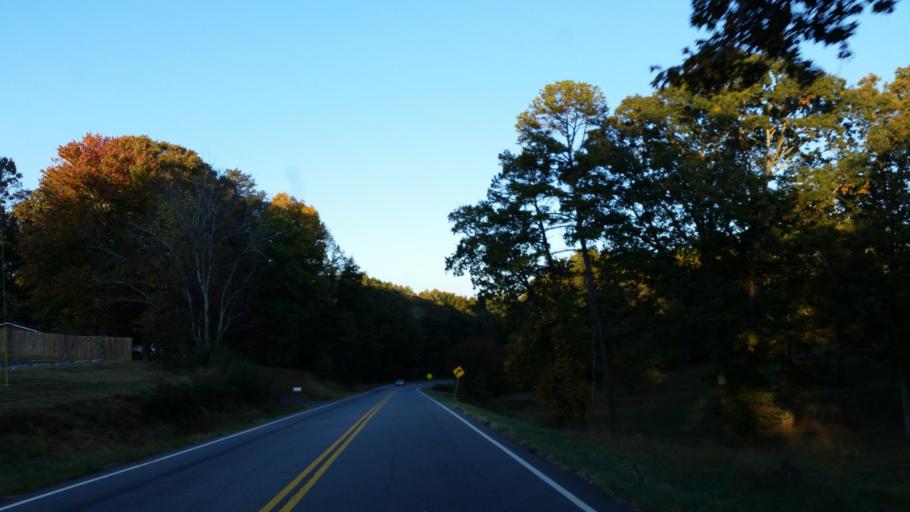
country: US
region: Georgia
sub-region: Lumpkin County
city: Dahlonega
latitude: 34.5236
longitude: -84.0373
